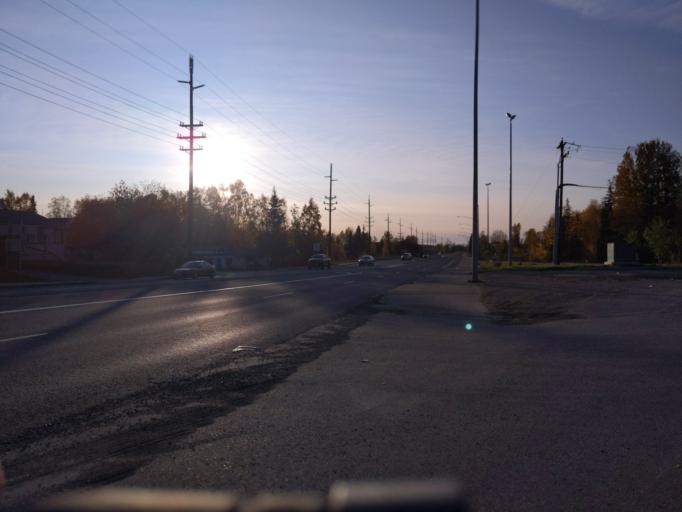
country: US
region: Alaska
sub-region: Anchorage Municipality
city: Anchorage
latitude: 61.1665
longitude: -149.8706
